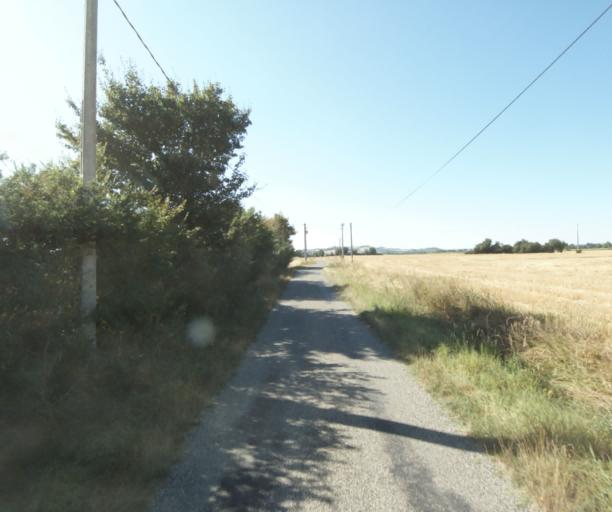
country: FR
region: Midi-Pyrenees
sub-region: Departement de la Haute-Garonne
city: Revel
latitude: 43.4695
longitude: 1.9712
